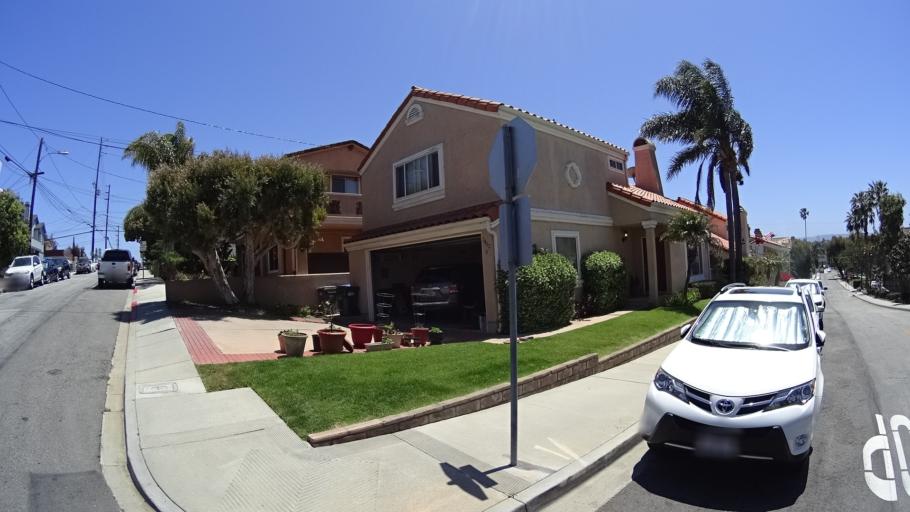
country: US
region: California
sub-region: Los Angeles County
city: Hermosa Beach
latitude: 33.8718
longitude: -118.3800
